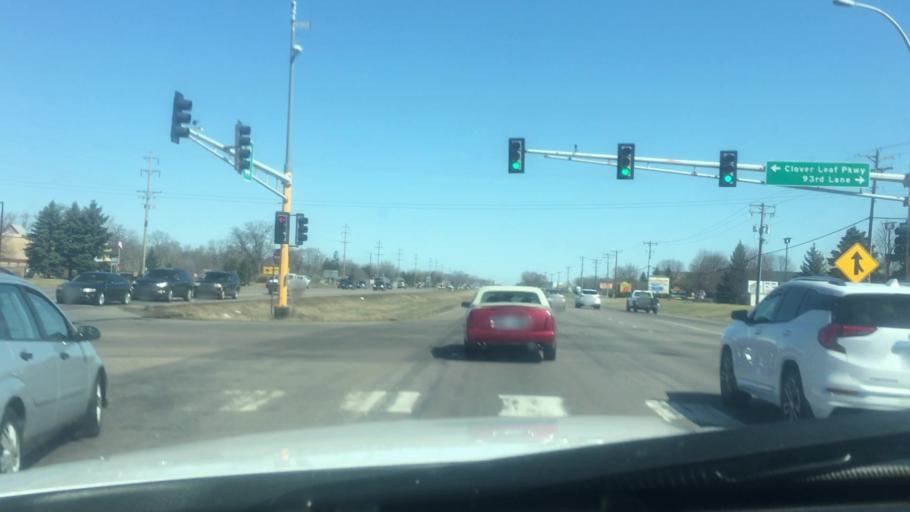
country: US
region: Minnesota
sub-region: Anoka County
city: Blaine
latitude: 45.1400
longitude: -93.2351
